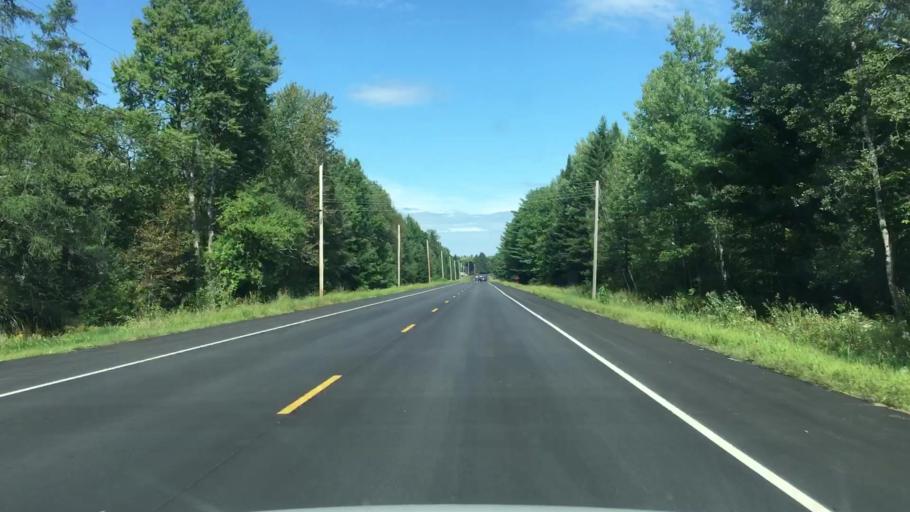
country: US
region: Maine
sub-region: Penobscot County
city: Corinna
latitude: 44.9626
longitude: -69.2697
